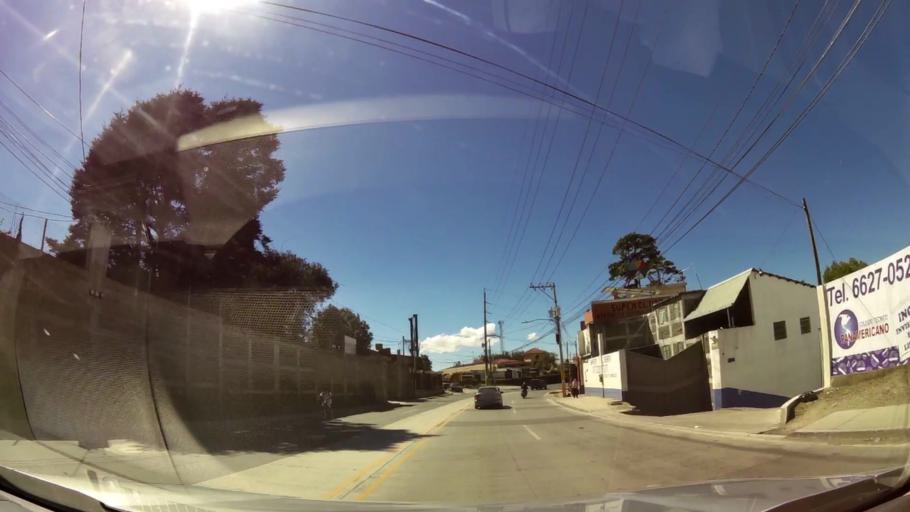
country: GT
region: Guatemala
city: San Jose Pinula
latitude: 14.5453
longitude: -90.4269
